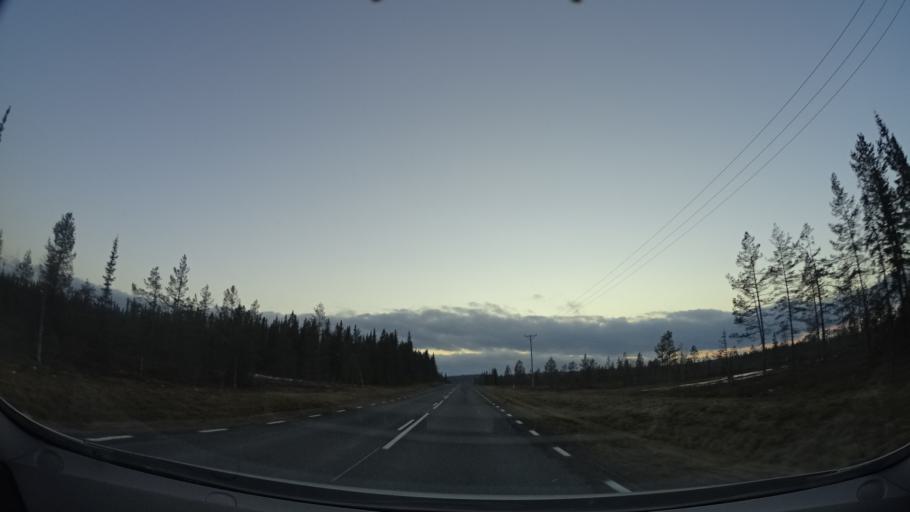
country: SE
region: Vaesterbotten
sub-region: Lycksele Kommun
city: Soderfors
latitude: 64.4136
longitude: 18.0250
